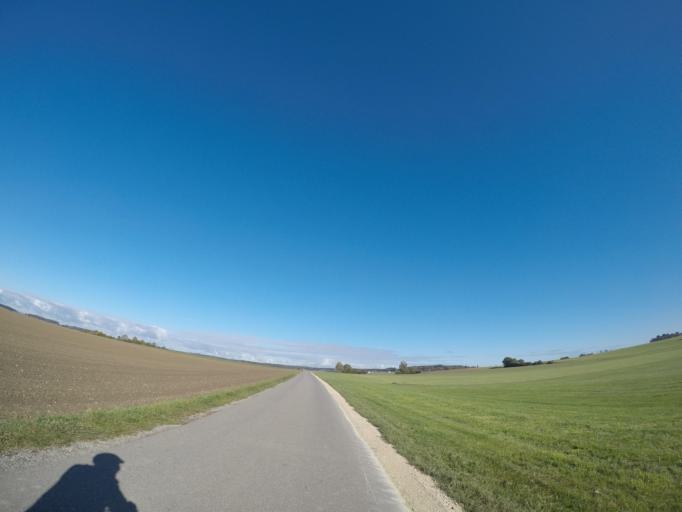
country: DE
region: Baden-Wuerttemberg
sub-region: Tuebingen Region
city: Saulgau
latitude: 48.0351
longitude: 9.5176
